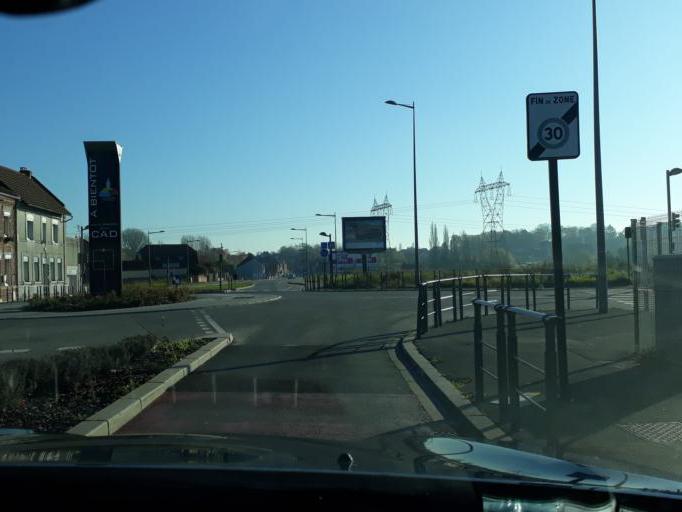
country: FR
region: Nord-Pas-de-Calais
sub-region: Departement du Nord
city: Guesnain
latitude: 50.3433
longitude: 3.1569
